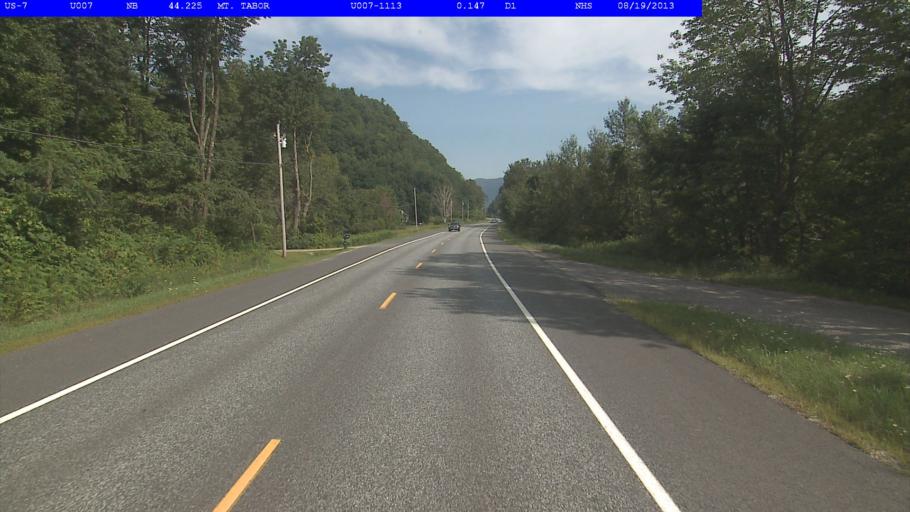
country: US
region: Vermont
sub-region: Bennington County
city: Manchester Center
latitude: 43.3072
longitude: -72.9946
